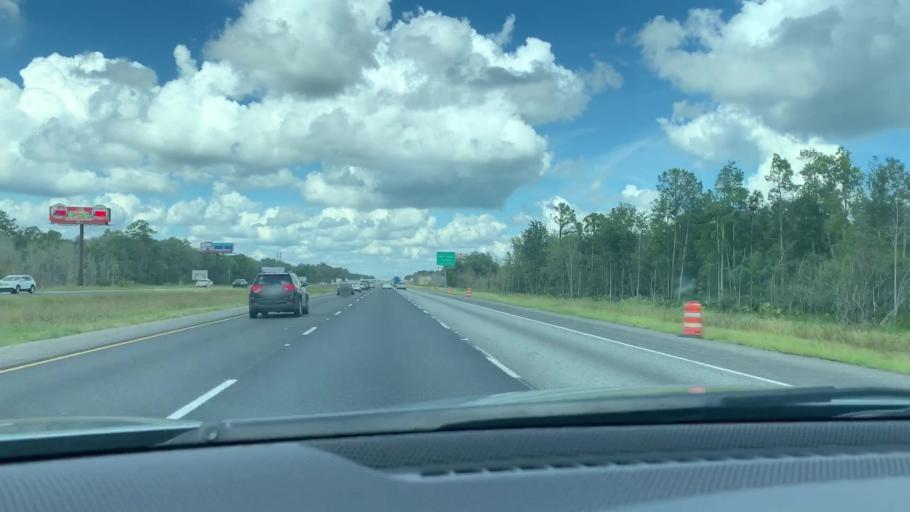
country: US
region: Georgia
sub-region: Camden County
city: Kingsland
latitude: 30.8117
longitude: -81.6632
